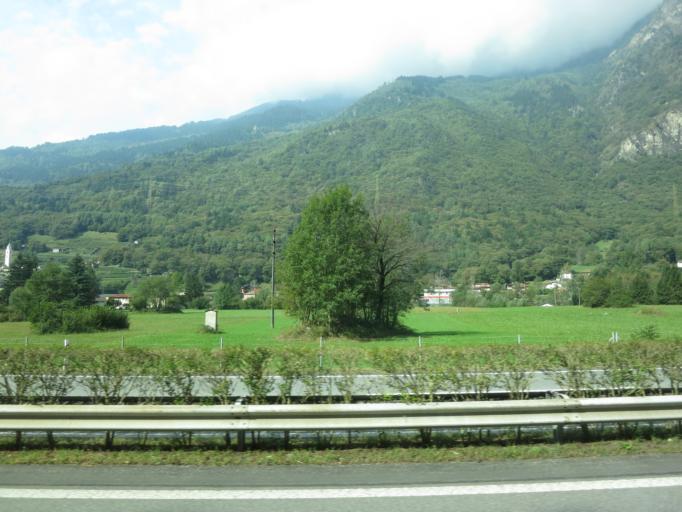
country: CH
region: Grisons
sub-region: Moesa District
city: Santa Maria in Calanca
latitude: 46.2728
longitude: 9.1756
